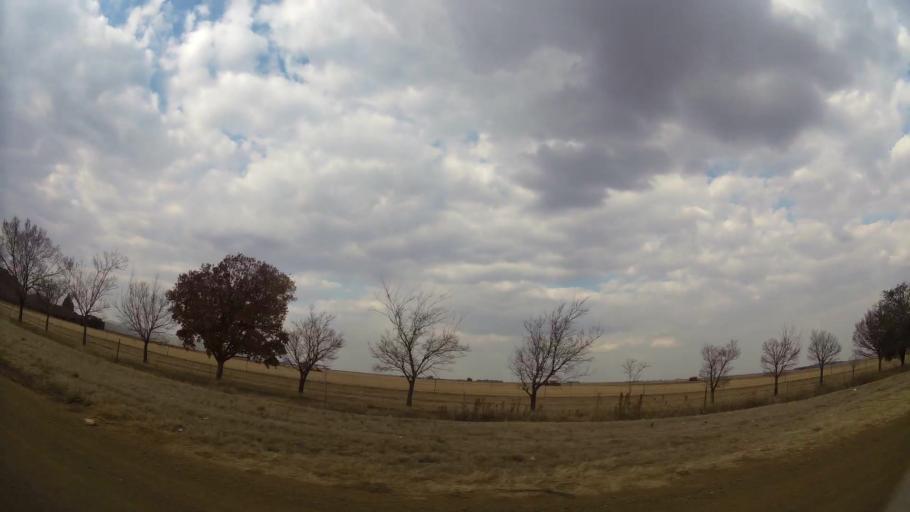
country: ZA
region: Mpumalanga
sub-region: Nkangala District Municipality
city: Delmas
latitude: -26.3075
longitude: 28.6059
